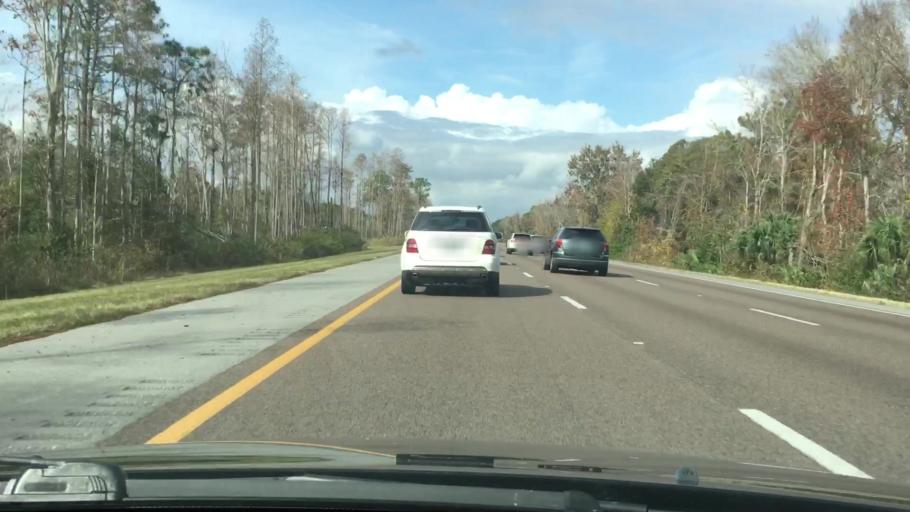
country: US
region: Florida
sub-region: Volusia County
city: Glencoe
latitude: 28.9783
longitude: -80.9651
